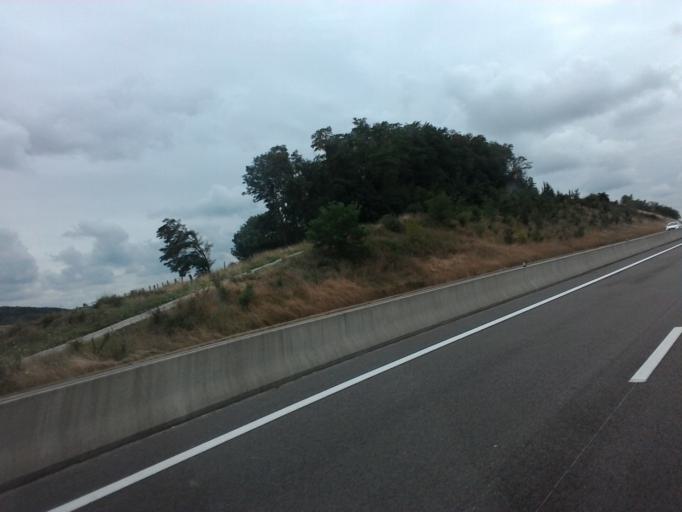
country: FR
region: Franche-Comte
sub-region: Departement du Jura
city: Montmorot
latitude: 46.6973
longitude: 5.5315
